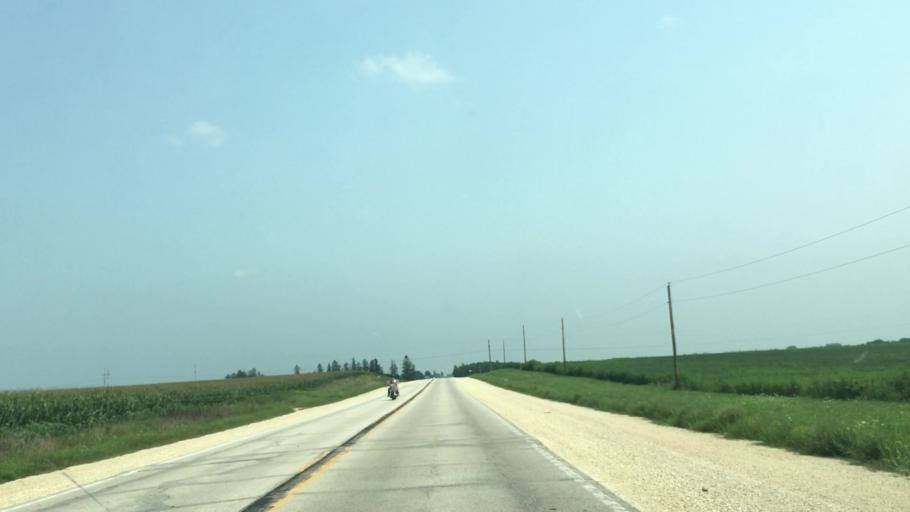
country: US
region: Iowa
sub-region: Fayette County
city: Oelwein
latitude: 42.6798
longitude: -91.8591
